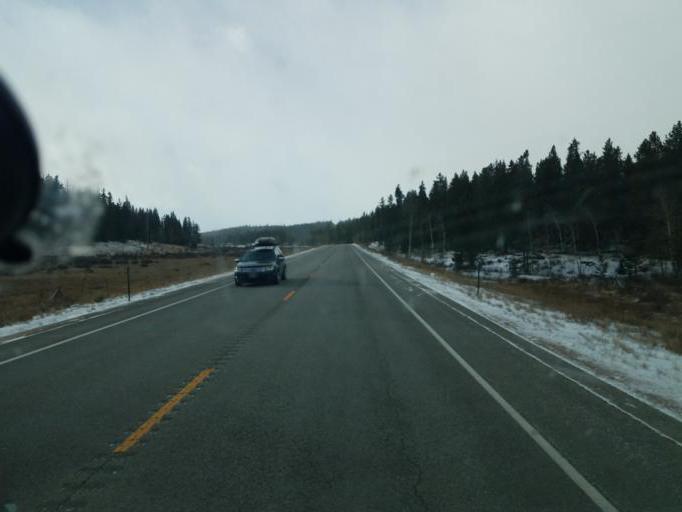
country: US
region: Colorado
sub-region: Summit County
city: Breckenridge
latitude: 39.4246
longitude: -105.7651
